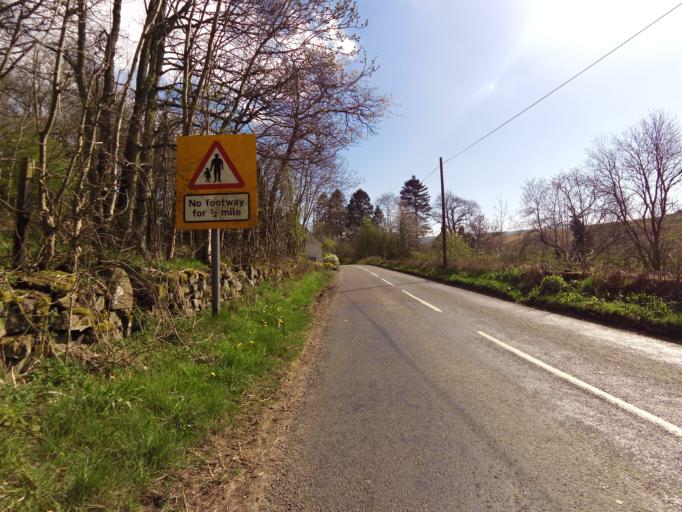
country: GB
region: Scotland
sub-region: Fife
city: Auchtermuchty
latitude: 56.3034
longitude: -3.2407
